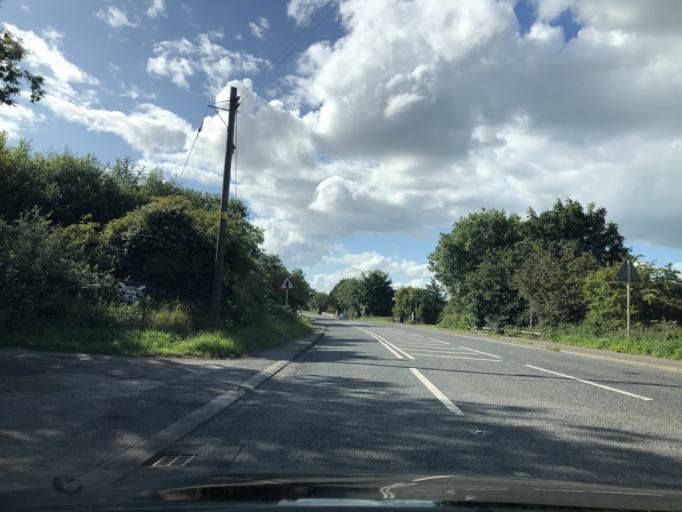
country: GB
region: Northern Ireland
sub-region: Ards District
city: Comber
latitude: 54.5683
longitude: -5.7695
